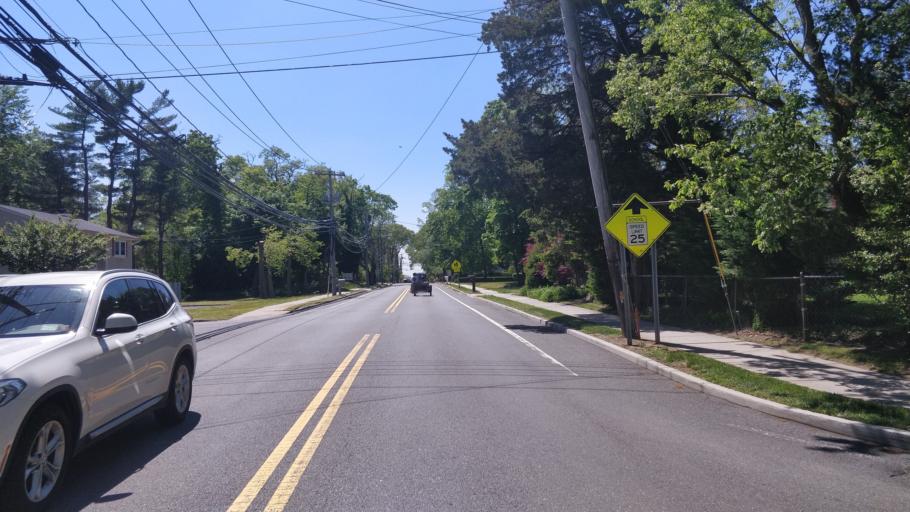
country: US
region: New York
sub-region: Suffolk County
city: Hauppauge
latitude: 40.8259
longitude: -73.1948
